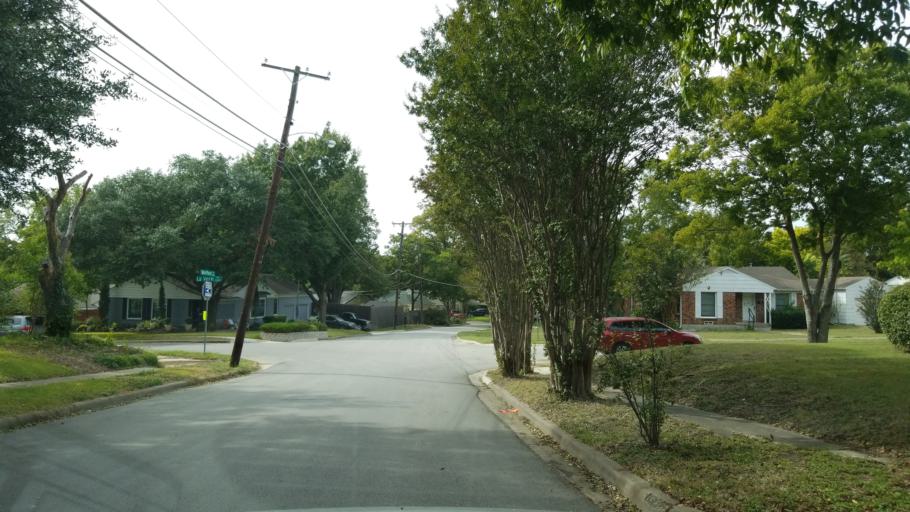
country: US
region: Texas
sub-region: Dallas County
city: Dallas
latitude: 32.7702
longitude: -96.7194
